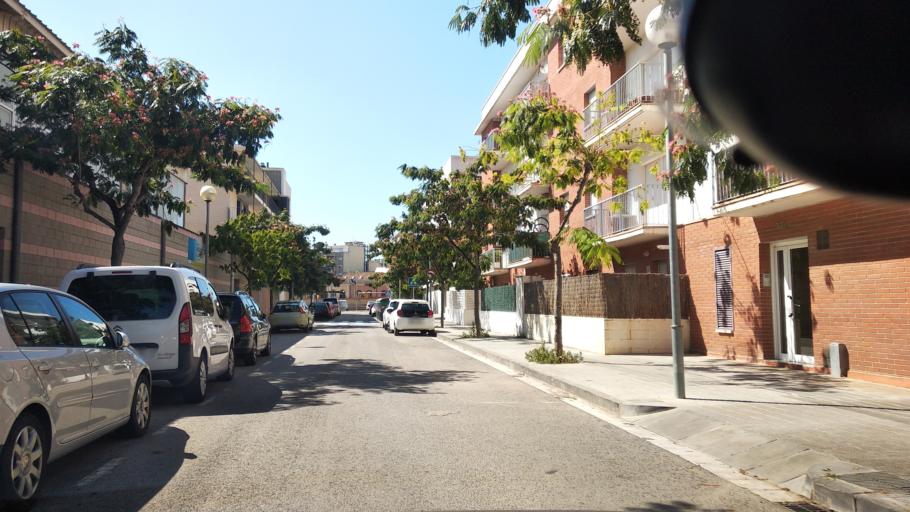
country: ES
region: Catalonia
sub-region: Provincia de Tarragona
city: El Vendrell
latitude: 41.2202
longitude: 1.5400
